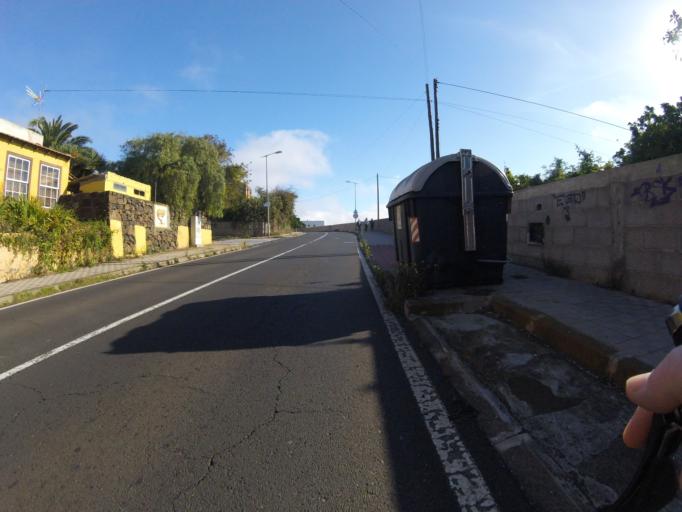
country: ES
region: Canary Islands
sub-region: Provincia de Santa Cruz de Tenerife
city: La Laguna
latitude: 28.4708
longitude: -16.3169
